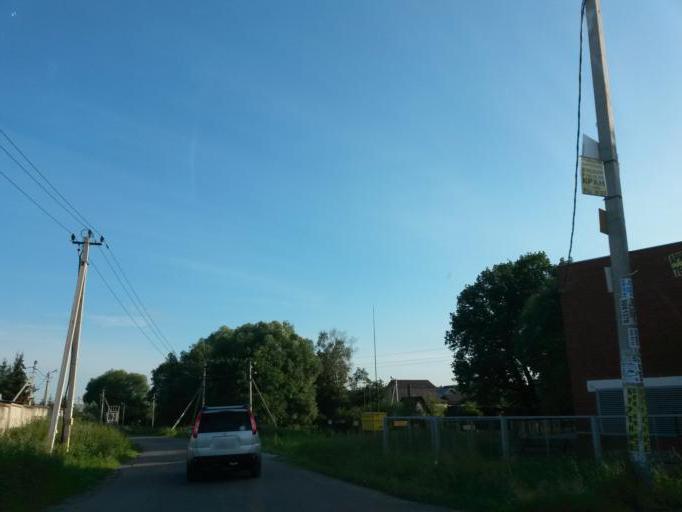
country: RU
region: Moskovskaya
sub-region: Podol'skiy Rayon
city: Podol'sk
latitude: 55.3951
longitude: 37.6200
